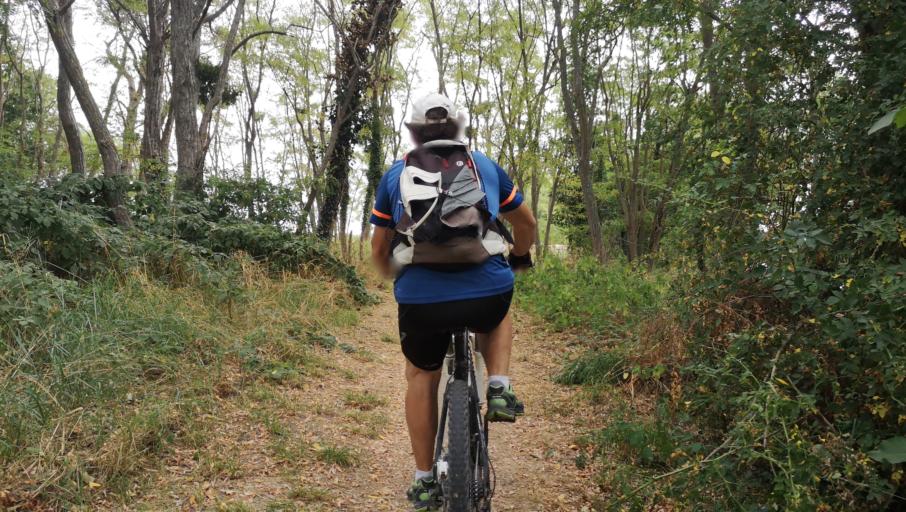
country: FR
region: Centre
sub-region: Departement du Loiret
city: Sandillon
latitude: 47.8612
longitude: 2.0502
